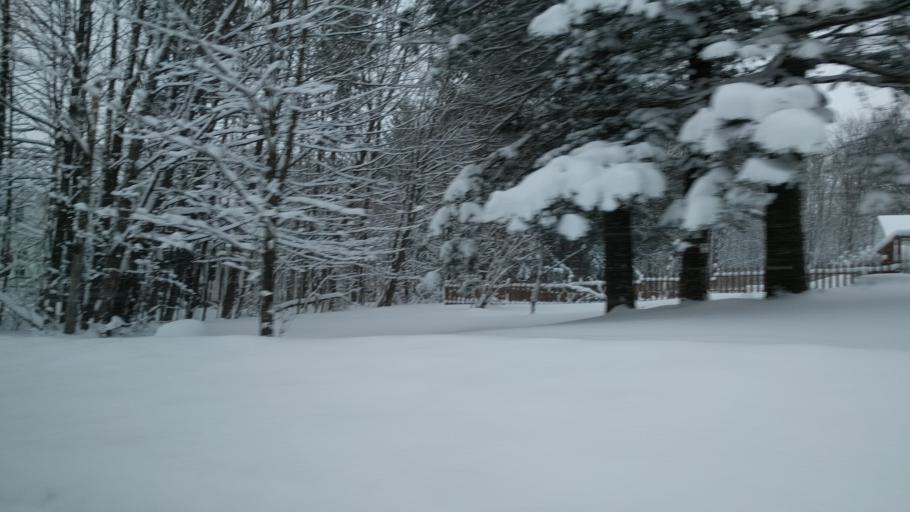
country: US
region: Wisconsin
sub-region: Iron County
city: Hurley
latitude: 46.4283
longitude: -90.2428
